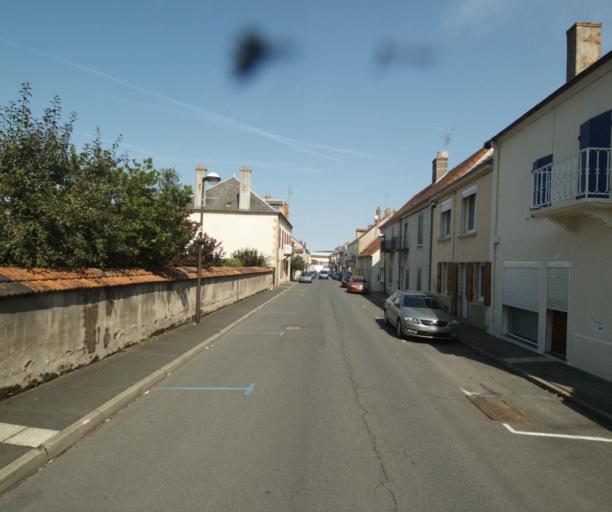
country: FR
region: Bourgogne
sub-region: Departement de Saone-et-Loire
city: Gueugnon
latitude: 46.5991
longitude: 4.0675
